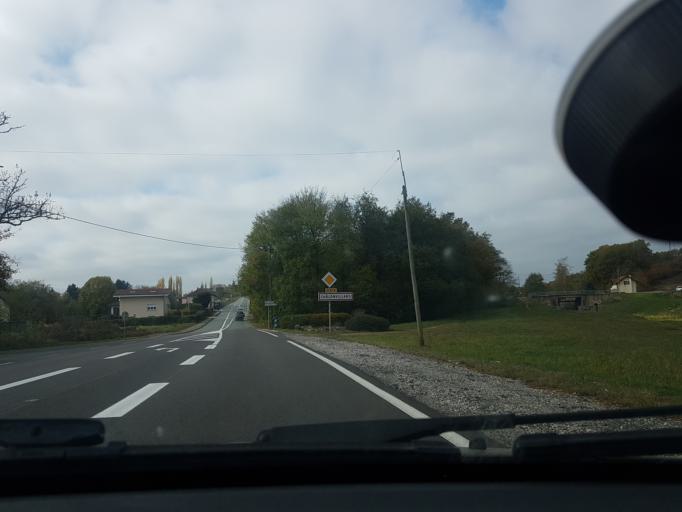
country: FR
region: Franche-Comte
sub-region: Departement de la Haute-Saone
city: Chalonvillars
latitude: 47.6416
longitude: 6.7958
